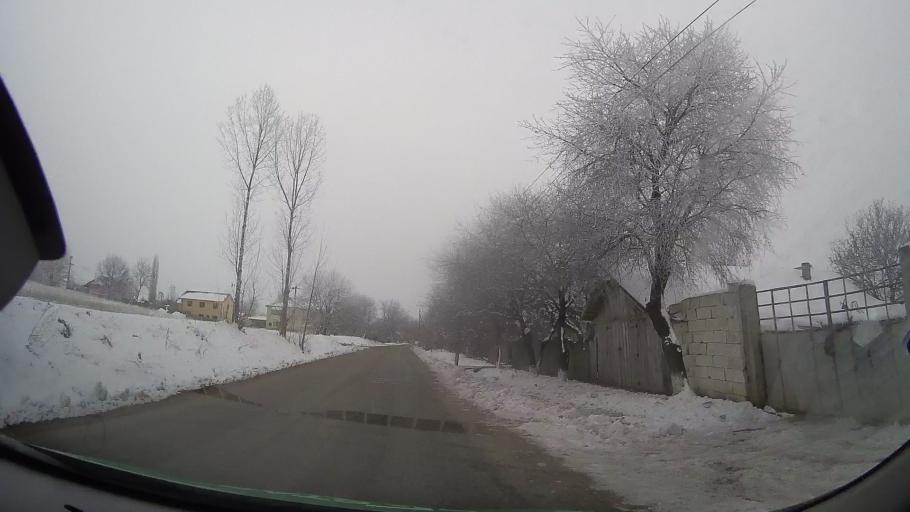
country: RO
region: Bacau
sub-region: Comuna Stanisesti
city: Stanisesti
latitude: 46.4076
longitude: 27.2720
